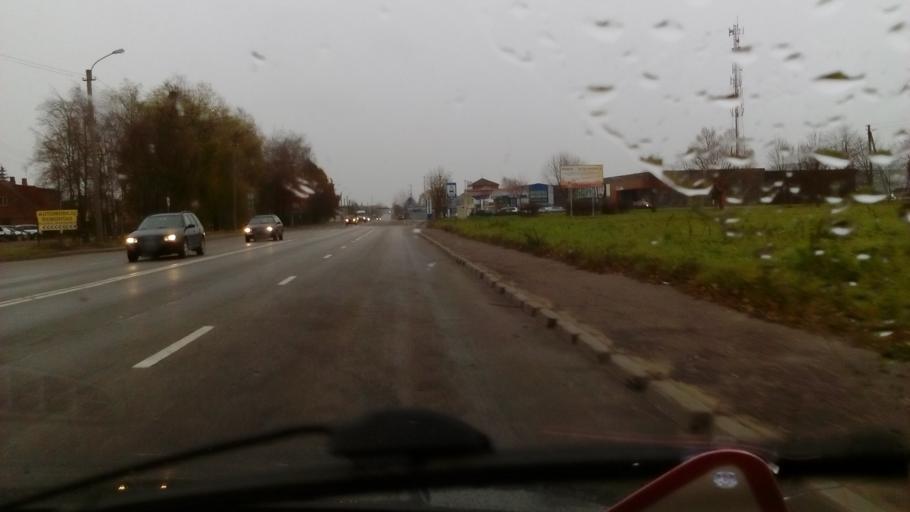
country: LT
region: Marijampoles apskritis
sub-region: Marijampole Municipality
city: Marijampole
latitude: 54.5544
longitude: 23.3684
